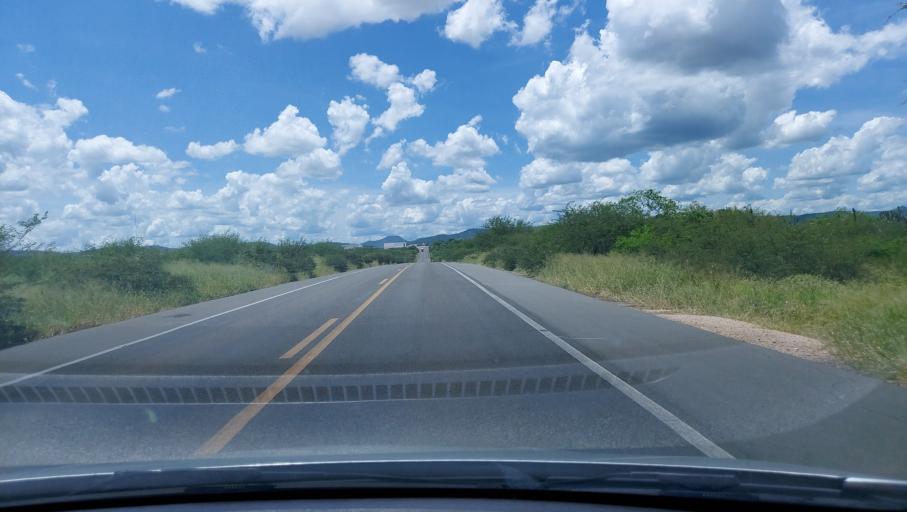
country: BR
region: Bahia
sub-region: Itaberaba
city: Itaberaba
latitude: -12.5212
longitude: -40.2672
